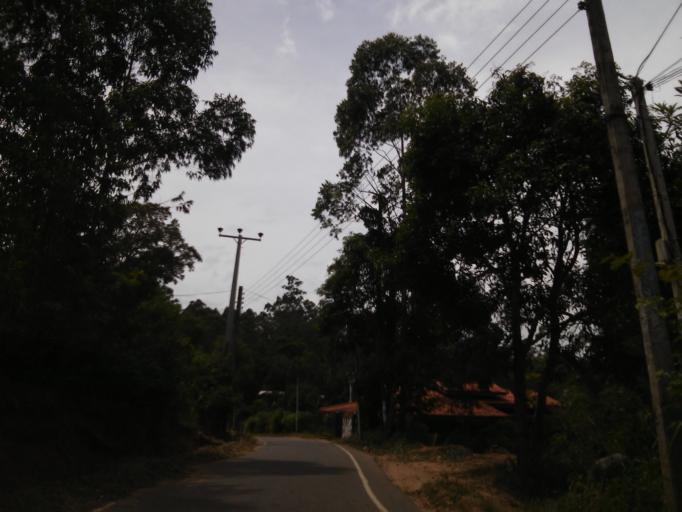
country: LK
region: Uva
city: Haputale
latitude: 6.8503
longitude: 81.0279
